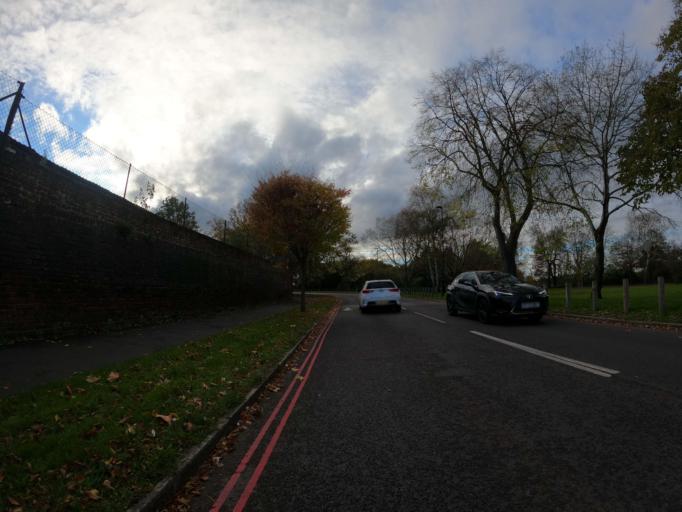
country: GB
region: England
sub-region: Greater London
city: Isleworth
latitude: 51.4890
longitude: -0.3397
